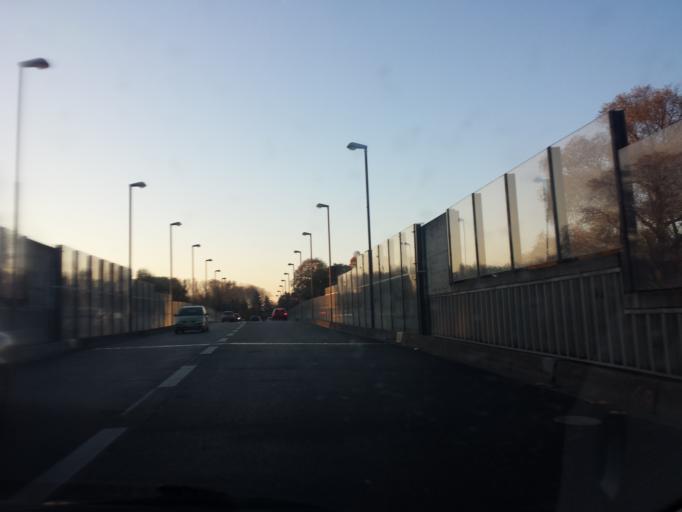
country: DE
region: Bavaria
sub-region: Upper Bavaria
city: Ingolstadt
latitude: 48.7564
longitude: 11.4258
